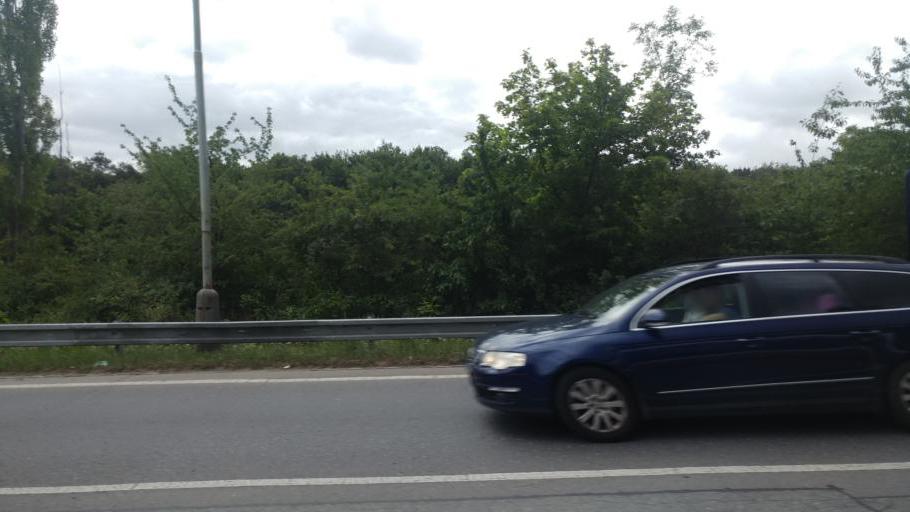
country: CZ
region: Praha
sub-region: Praha 9
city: Vysocany
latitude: 50.0904
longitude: 14.5049
